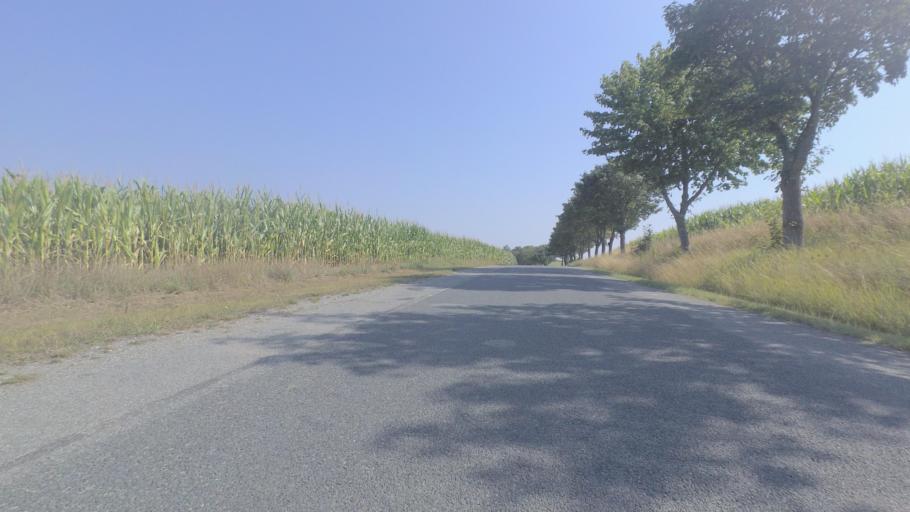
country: DE
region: Mecklenburg-Vorpommern
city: Pampow
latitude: 53.7042
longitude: 12.6116
